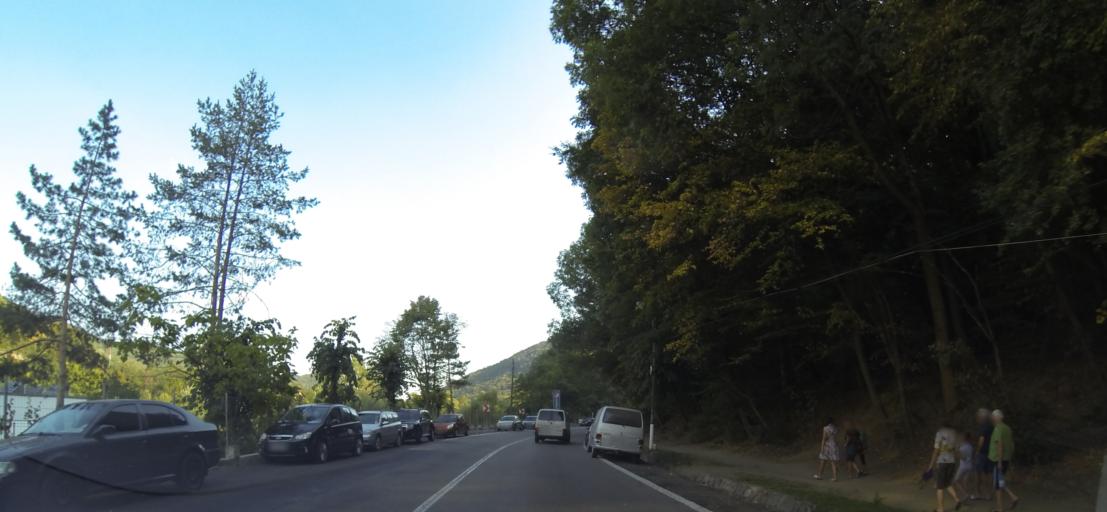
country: RO
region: Valcea
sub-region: Oras Calimanesti
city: Calimanesti
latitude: 45.2655
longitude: 24.3197
